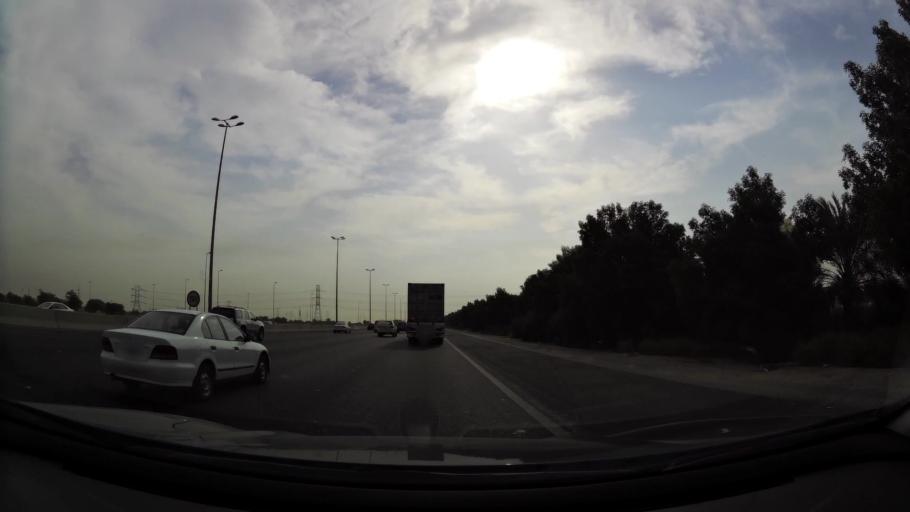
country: KW
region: Muhafazat al Jahra'
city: Al Jahra'
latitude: 29.3196
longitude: 47.7593
